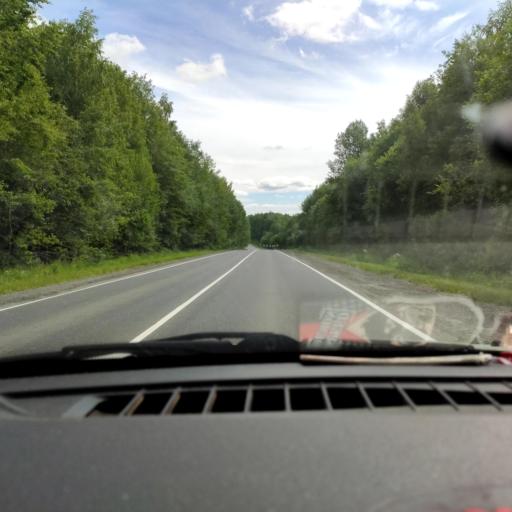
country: RU
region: Perm
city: Chusovoy
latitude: 58.3838
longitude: 57.9178
